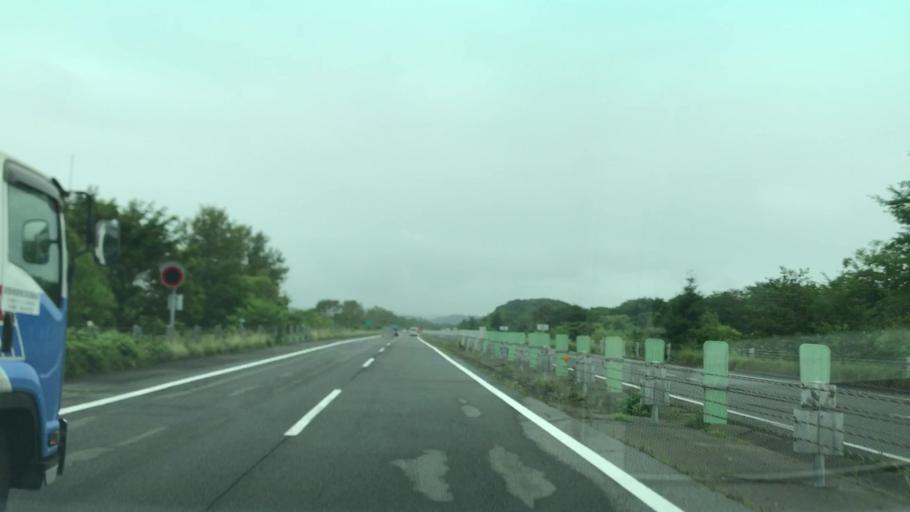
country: JP
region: Hokkaido
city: Shiraoi
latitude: 42.5187
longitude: 141.2692
